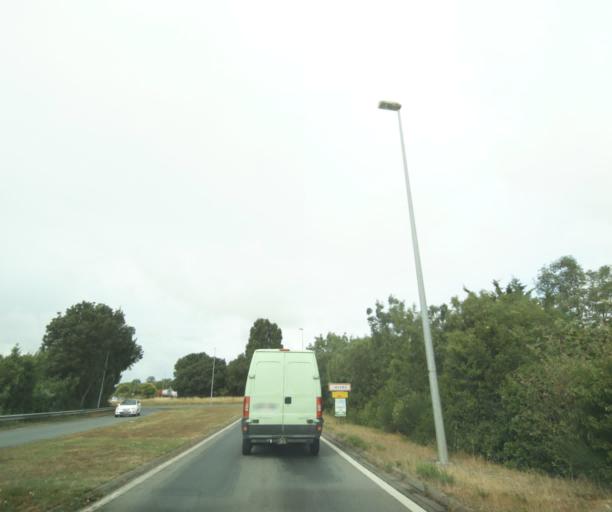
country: FR
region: Poitou-Charentes
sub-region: Departement de la Charente-Maritime
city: Lagord
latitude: 46.1911
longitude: -1.1455
